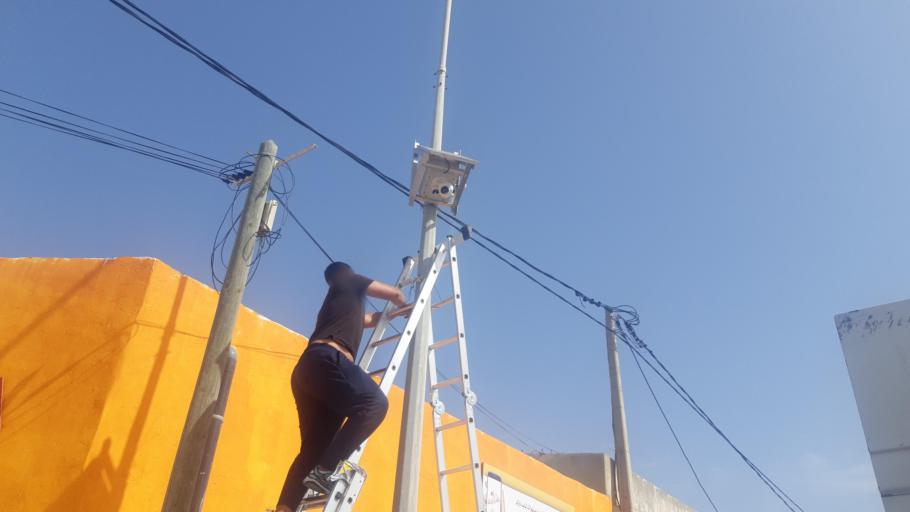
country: TN
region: Al Mahdiyah
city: Zouila
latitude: 35.4972
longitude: 11.0552
